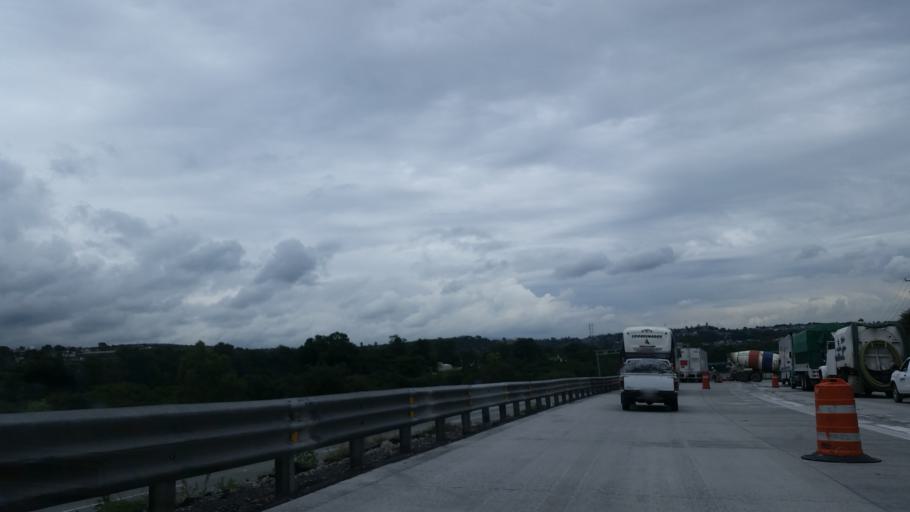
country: MX
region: Hidalgo
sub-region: Tepeji del Rio de Ocampo
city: Santiago Tlapanaloya
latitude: 19.8821
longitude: -99.3428
